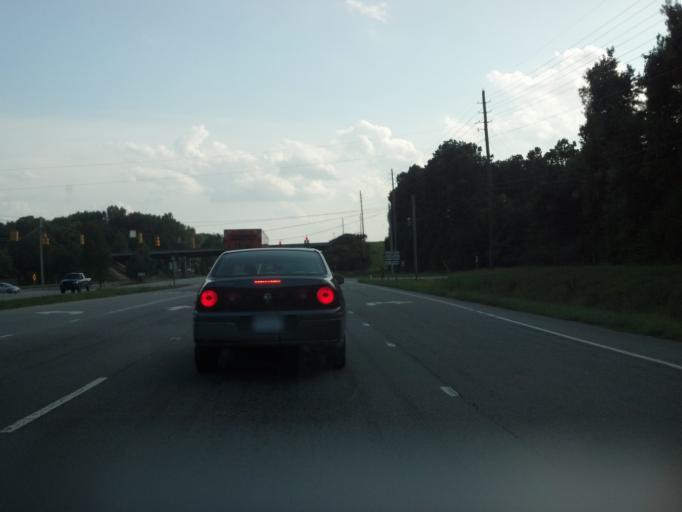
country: US
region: North Carolina
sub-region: Pitt County
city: Greenville
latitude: 35.6617
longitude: -77.3629
